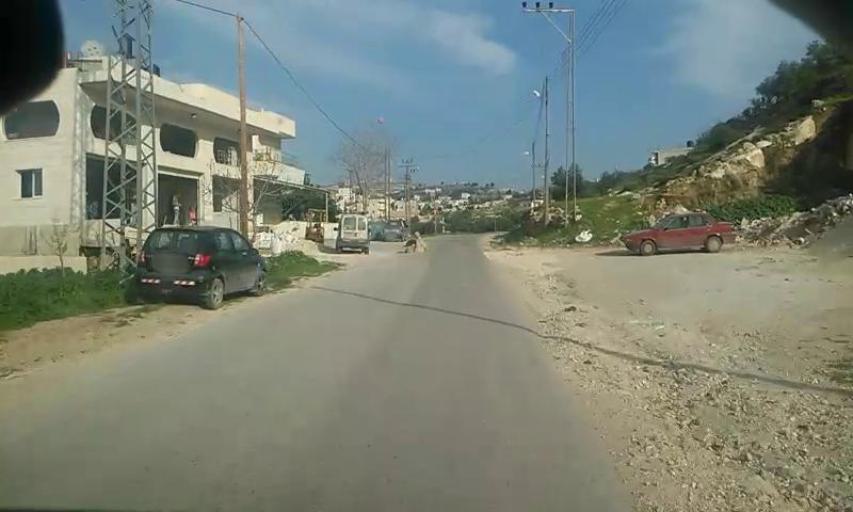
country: PS
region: West Bank
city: Nuba
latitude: 31.6139
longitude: 35.0324
